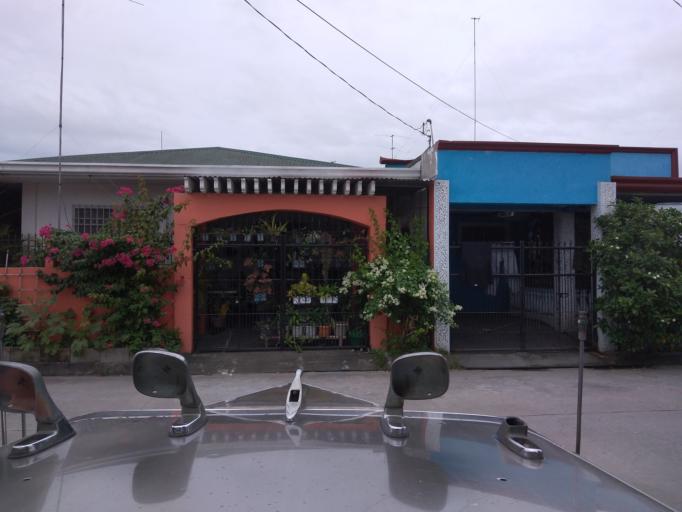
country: PH
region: Central Luzon
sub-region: Province of Pampanga
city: Pandacaqui
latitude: 15.1747
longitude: 120.6446
